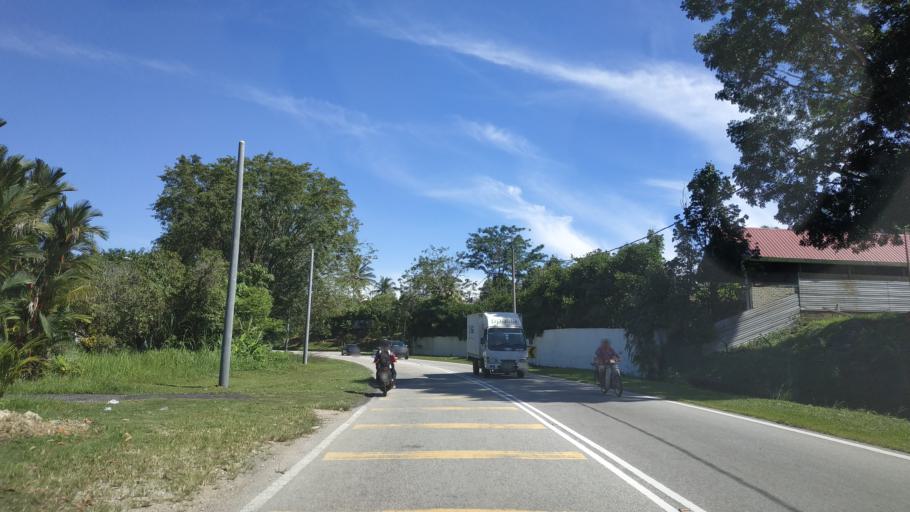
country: MY
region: Kedah
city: Kulim
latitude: 5.3438
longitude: 100.5380
